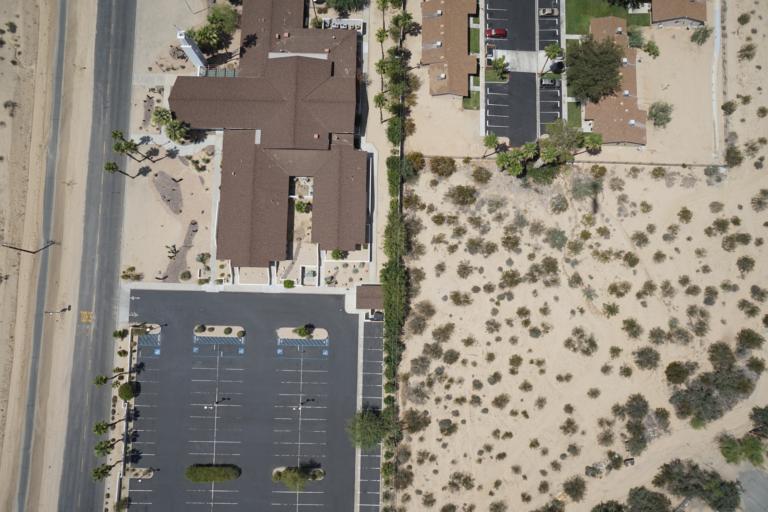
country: US
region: California
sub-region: San Bernardino County
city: Twentynine Palms
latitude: 34.1433
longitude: -116.0692
